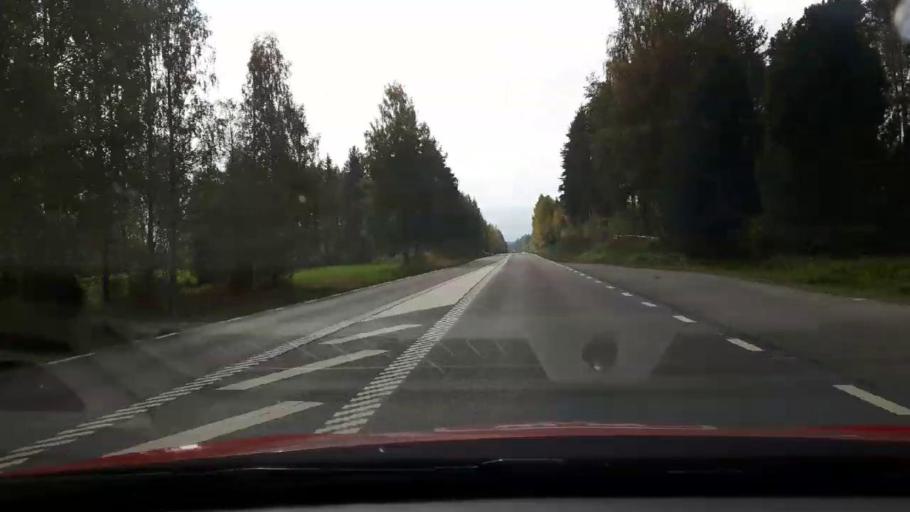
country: SE
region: Gaevleborg
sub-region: Bollnas Kommun
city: Arbra
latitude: 61.4826
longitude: 16.3660
